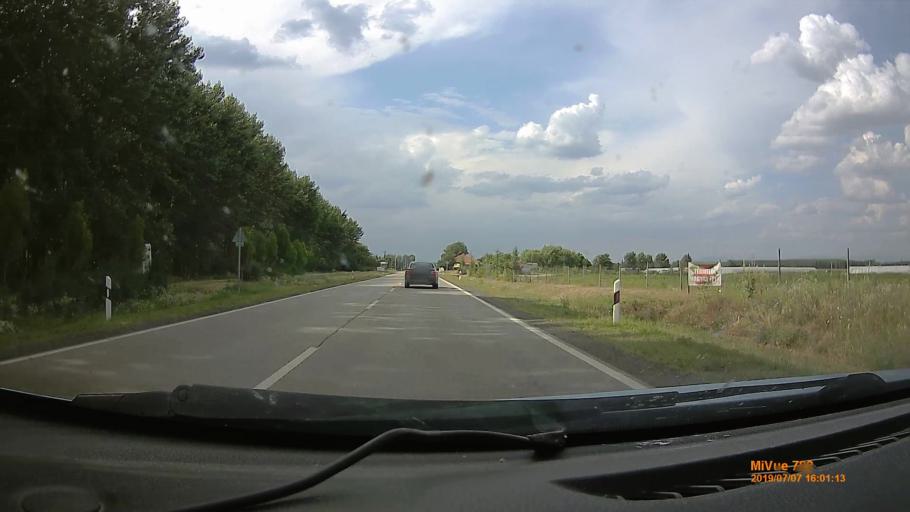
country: HU
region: Heves
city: Boldog
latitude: 47.6075
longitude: 19.7401
